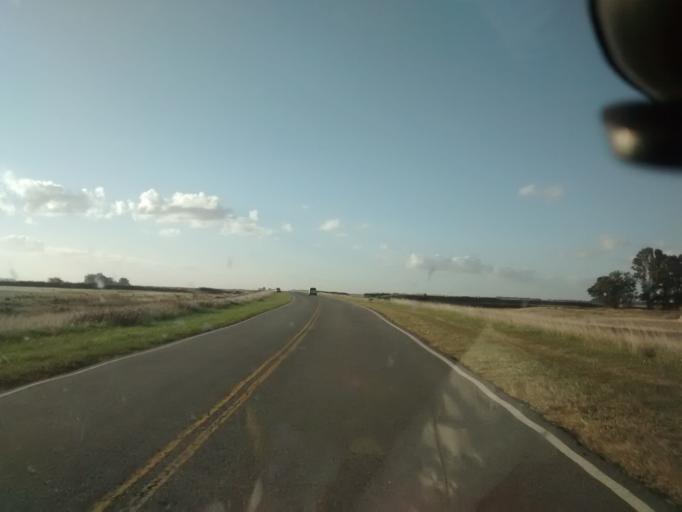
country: AR
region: Buenos Aires
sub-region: Partido de General Belgrano
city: General Belgrano
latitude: -36.0943
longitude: -58.6088
